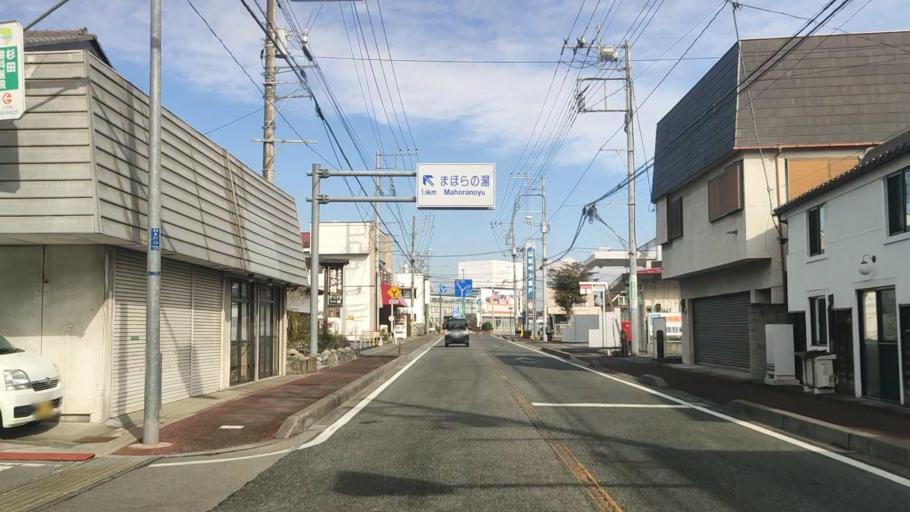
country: JP
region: Yamanashi
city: Ryuo
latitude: 35.5611
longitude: 138.4664
